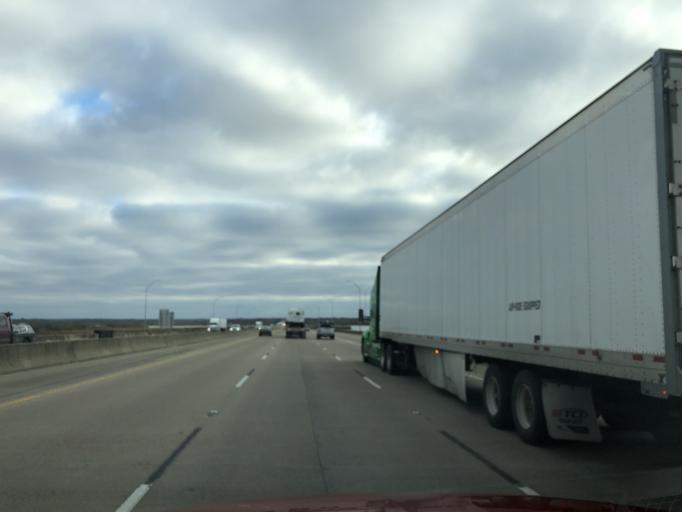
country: US
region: Texas
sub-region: Chambers County
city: Old River-Winfree
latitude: 29.8306
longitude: -94.8016
